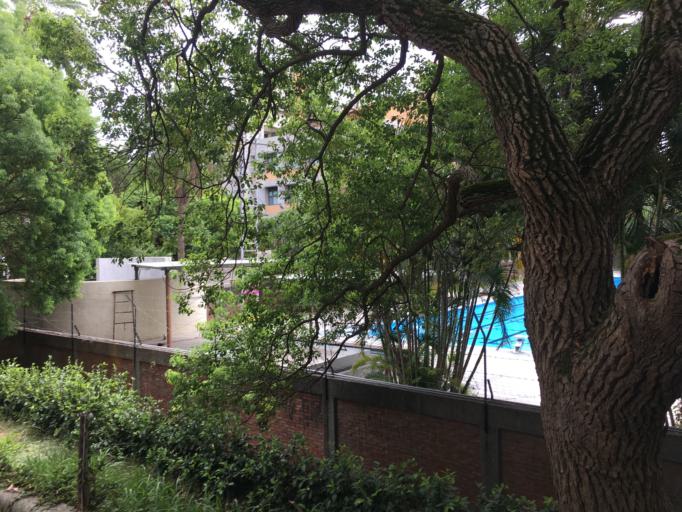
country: TW
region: Taiwan
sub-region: Hsinchu
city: Hsinchu
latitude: 24.7899
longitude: 120.9954
